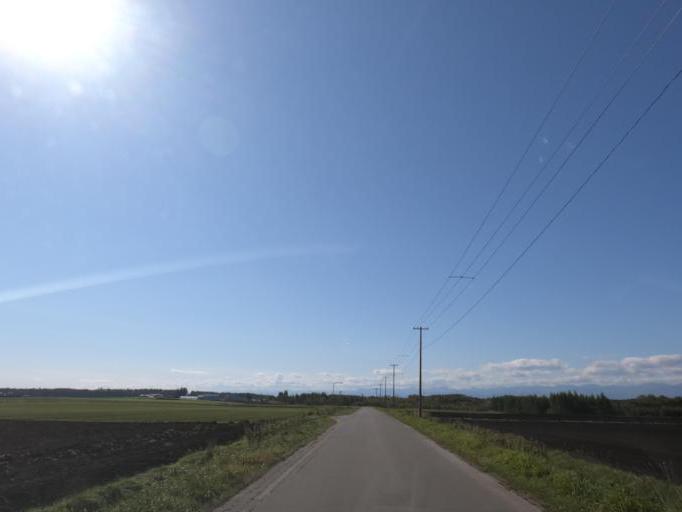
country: JP
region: Hokkaido
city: Obihiro
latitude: 42.8041
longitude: 143.2608
